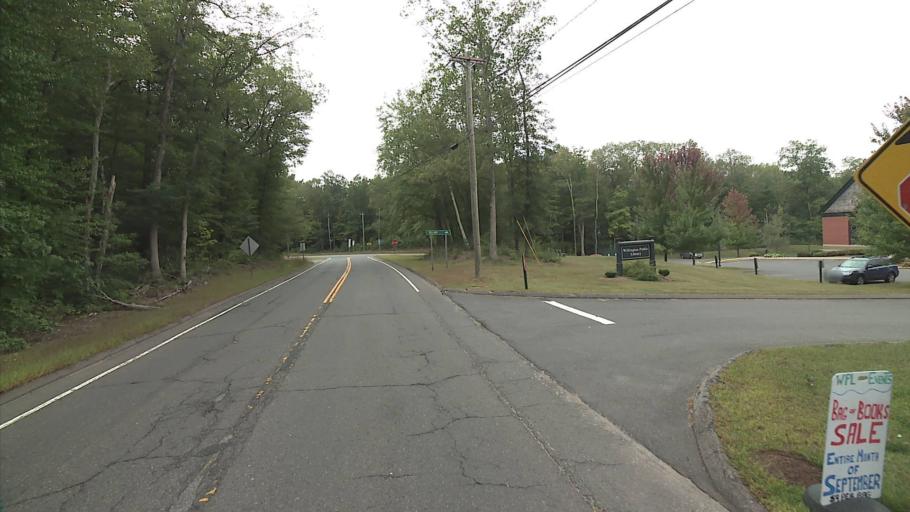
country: US
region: Connecticut
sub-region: Tolland County
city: Storrs
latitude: 41.8778
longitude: -72.2674
